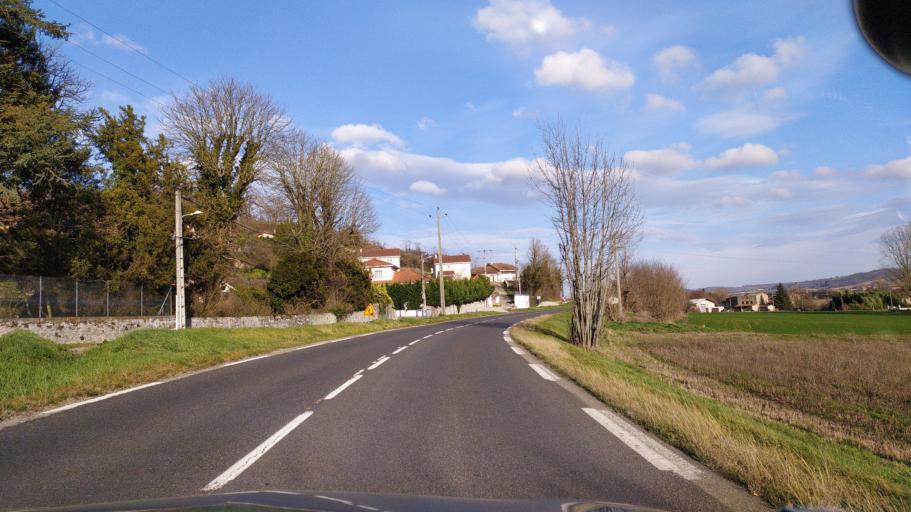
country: FR
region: Rhone-Alpes
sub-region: Departement de l'Isere
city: Pont-Eveque
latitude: 45.5372
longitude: 4.9083
